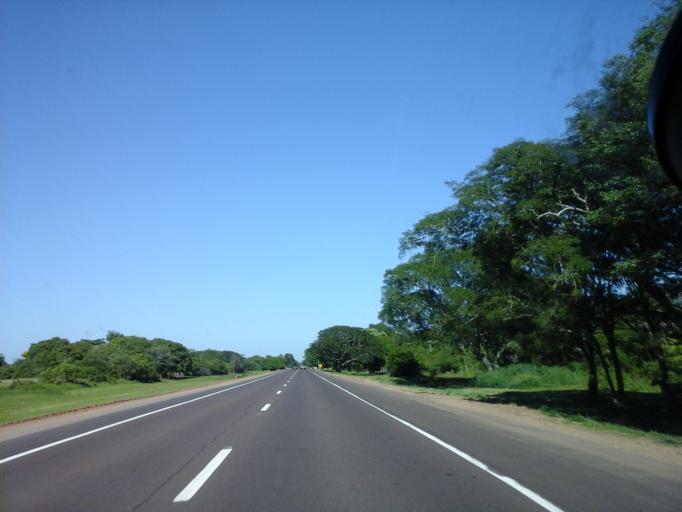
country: AR
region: Corrientes
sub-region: Departamento de San Cosme
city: San Cosme
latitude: -27.3683
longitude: -58.4093
